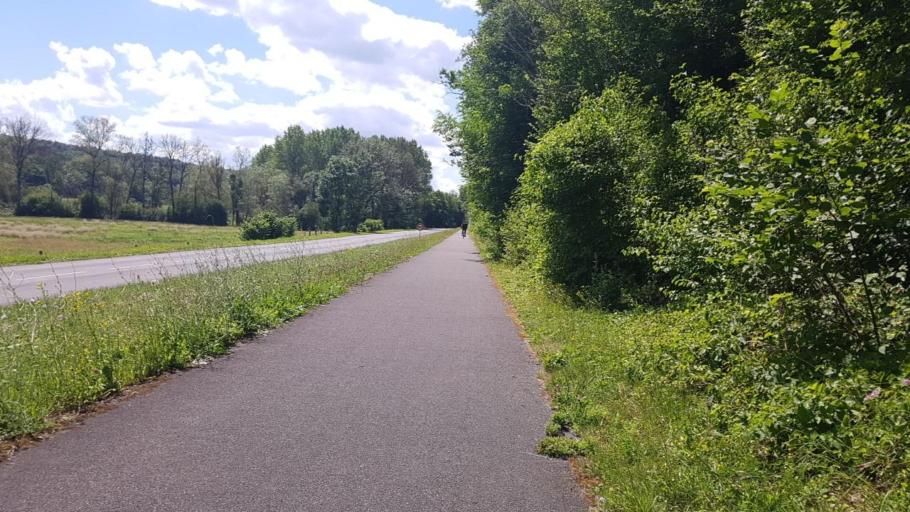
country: FR
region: Lorraine
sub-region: Departement de la Meuse
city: Vacon
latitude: 48.6757
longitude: 5.6094
